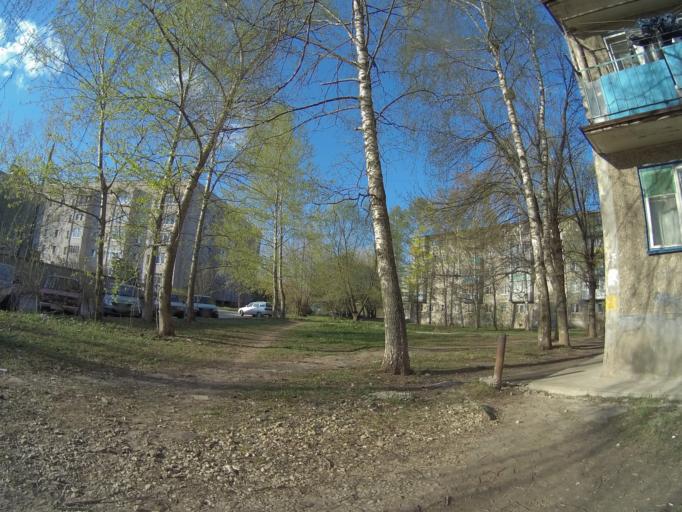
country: RU
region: Vladimir
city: Vladimir
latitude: 56.1374
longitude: 40.3587
